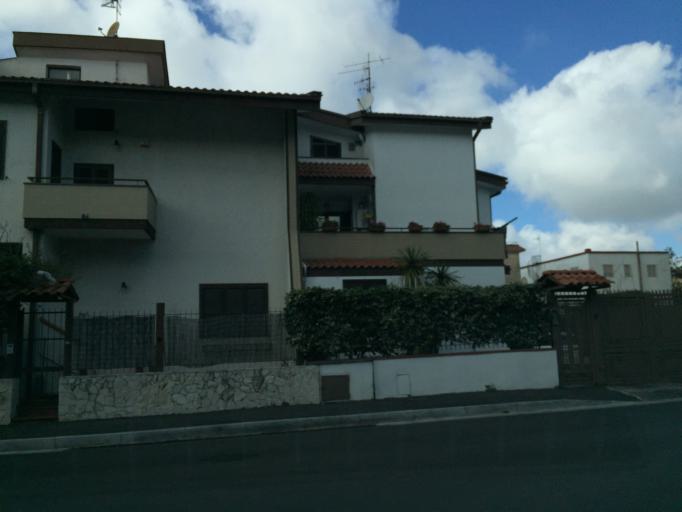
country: IT
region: Campania
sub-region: Provincia di Napoli
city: Massa di Somma
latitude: 40.8431
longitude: 14.3735
